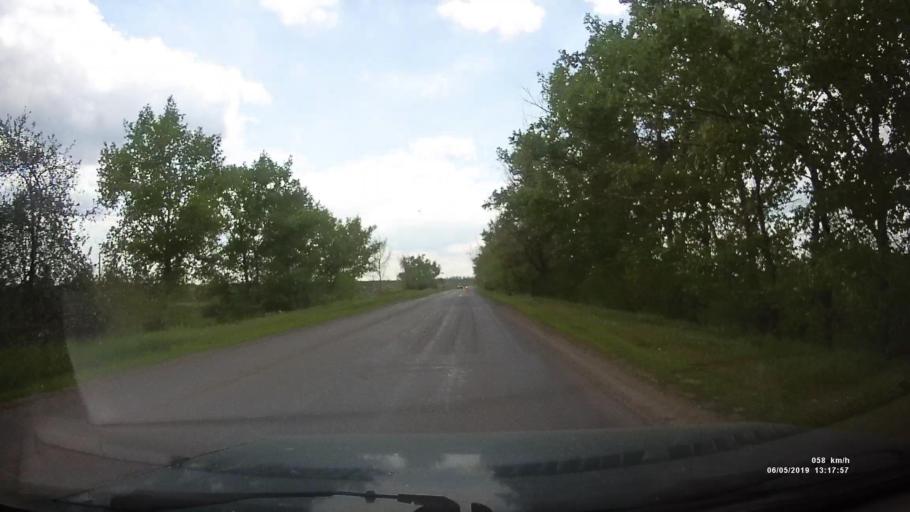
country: RU
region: Rostov
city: Ust'-Donetskiy
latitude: 47.7371
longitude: 40.9187
